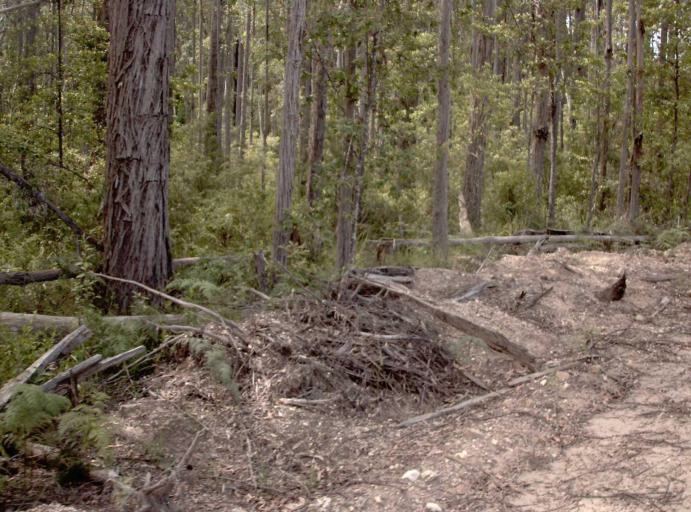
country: AU
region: Victoria
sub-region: East Gippsland
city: Lakes Entrance
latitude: -37.6269
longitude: 148.6779
